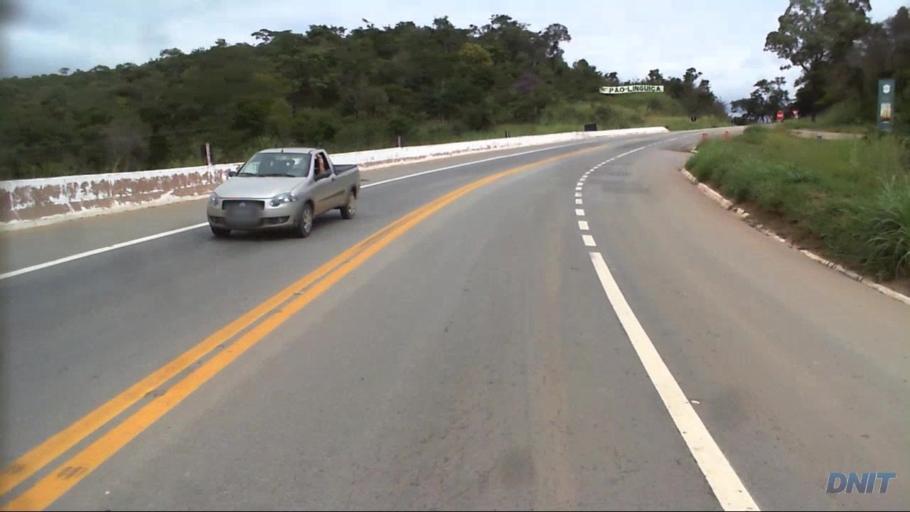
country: BR
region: Minas Gerais
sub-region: Caete
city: Caete
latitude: -19.7622
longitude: -43.6401
